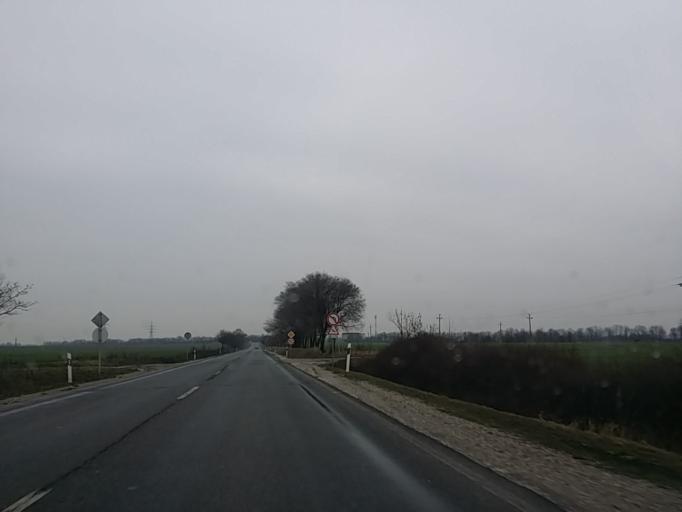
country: HU
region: Borsod-Abauj-Zemplen
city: Mezokovesd
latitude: 47.8232
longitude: 20.5857
